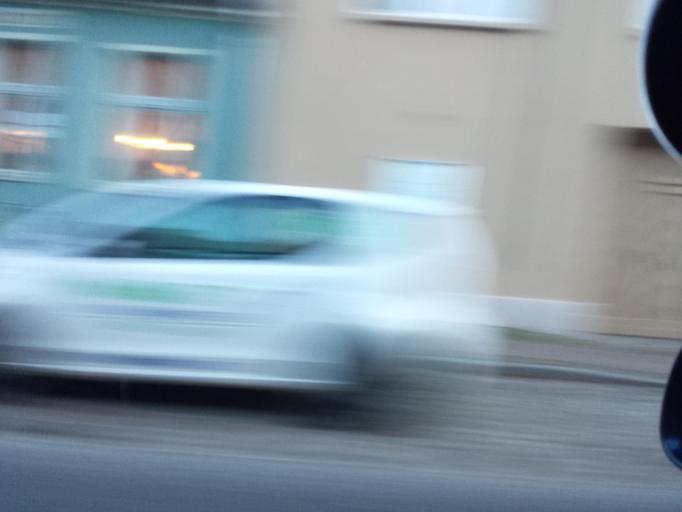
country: DE
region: Brandenburg
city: Kremmen
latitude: 52.7609
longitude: 13.0247
